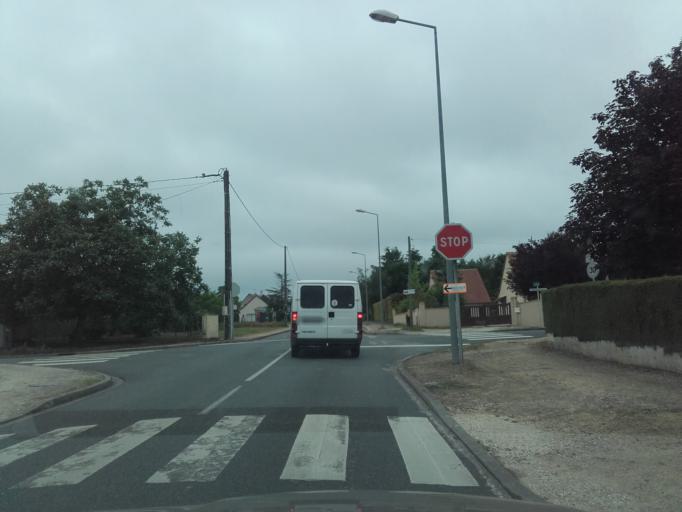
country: FR
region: Centre
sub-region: Departement d'Indre-et-Loire
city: Monnaie
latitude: 47.5082
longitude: 0.7923
